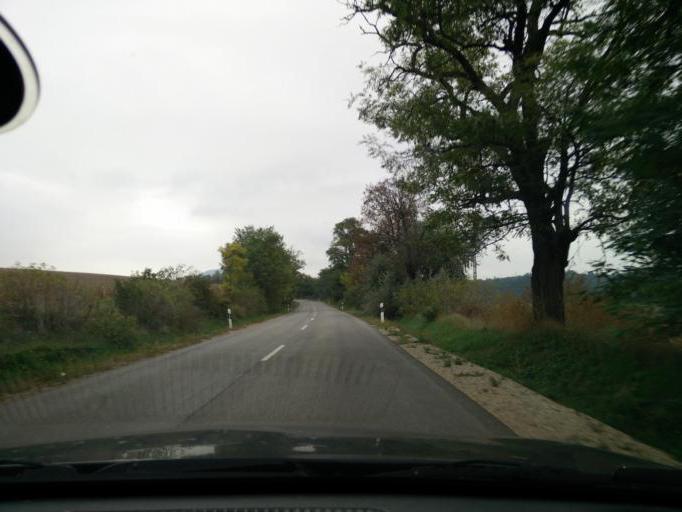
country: HU
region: Komarom-Esztergom
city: Tokod
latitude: 47.7014
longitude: 18.6250
